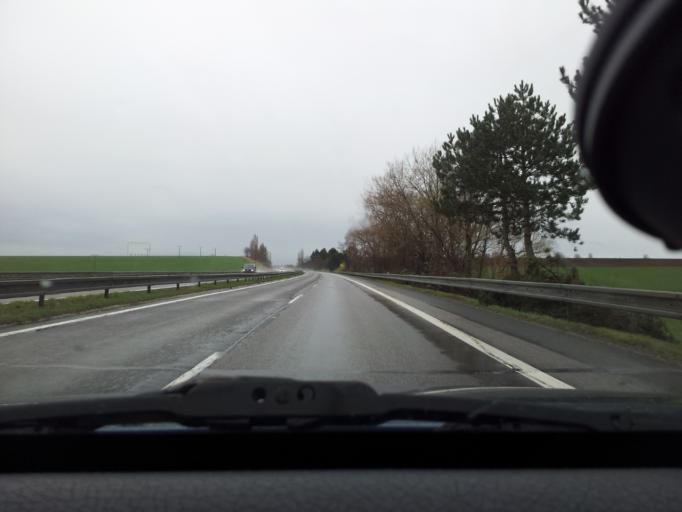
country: SK
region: Nitriansky
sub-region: Okres Nitra
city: Nitra
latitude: 48.3210
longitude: 17.9332
